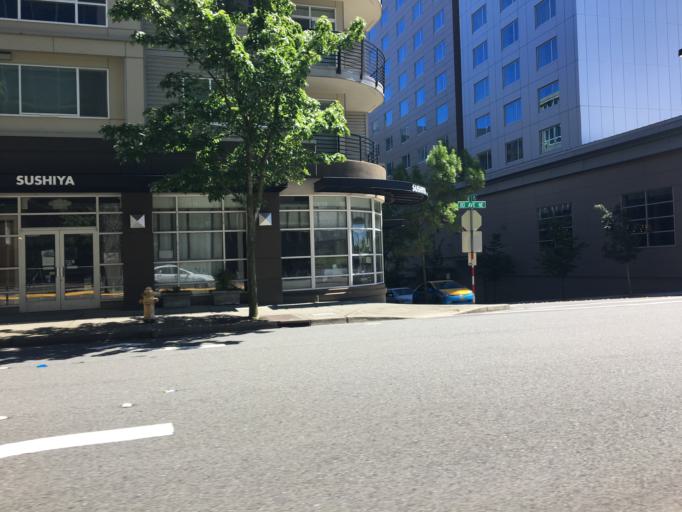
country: US
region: Washington
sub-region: King County
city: Bellevue
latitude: 47.6134
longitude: -122.1936
